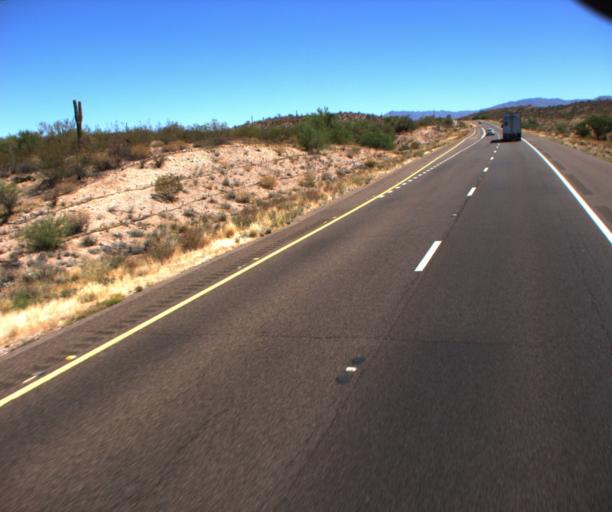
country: US
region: Arizona
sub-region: Maricopa County
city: Fountain Hills
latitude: 33.5919
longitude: -111.5954
